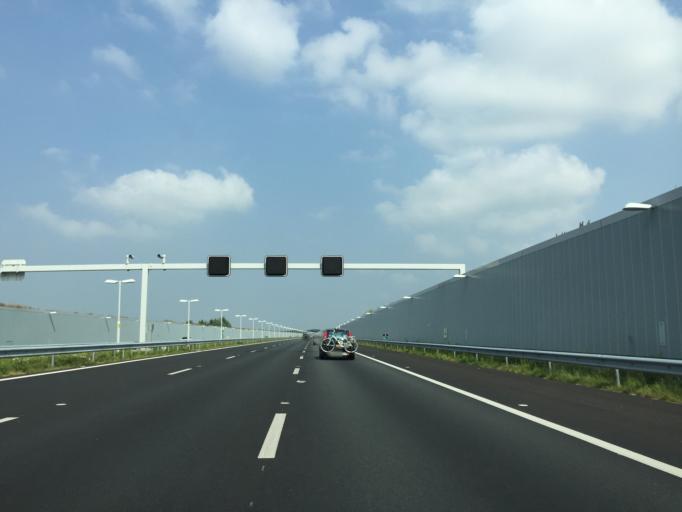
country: NL
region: South Holland
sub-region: Gemeente Vlaardingen
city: Vlaardingen
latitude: 51.9589
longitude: 4.3475
